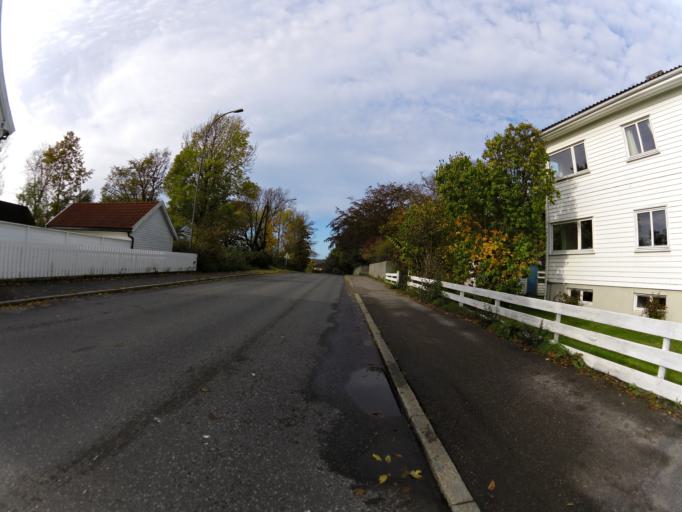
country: NO
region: Ostfold
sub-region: Fredrikstad
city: Fredrikstad
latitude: 59.2231
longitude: 10.9334
